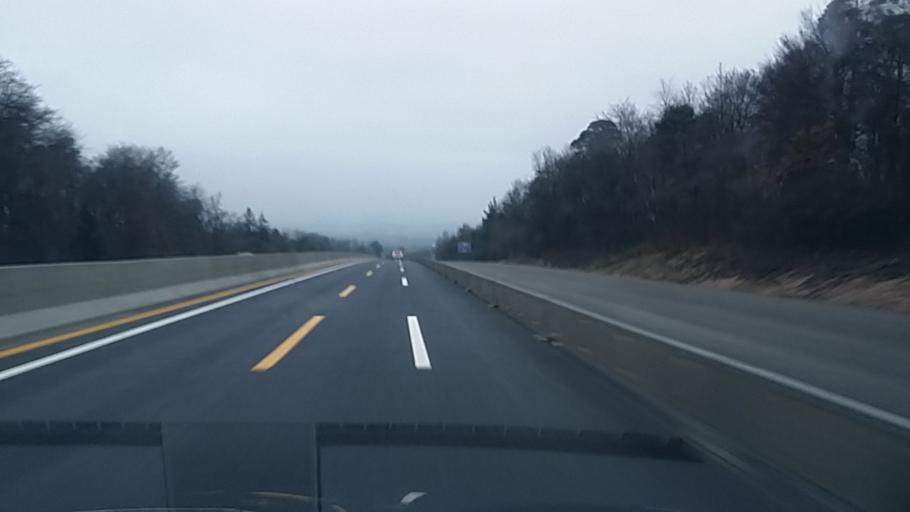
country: DE
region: Hesse
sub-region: Regierungsbezirk Kassel
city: Guxhagen
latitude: 51.1677
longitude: 9.4763
